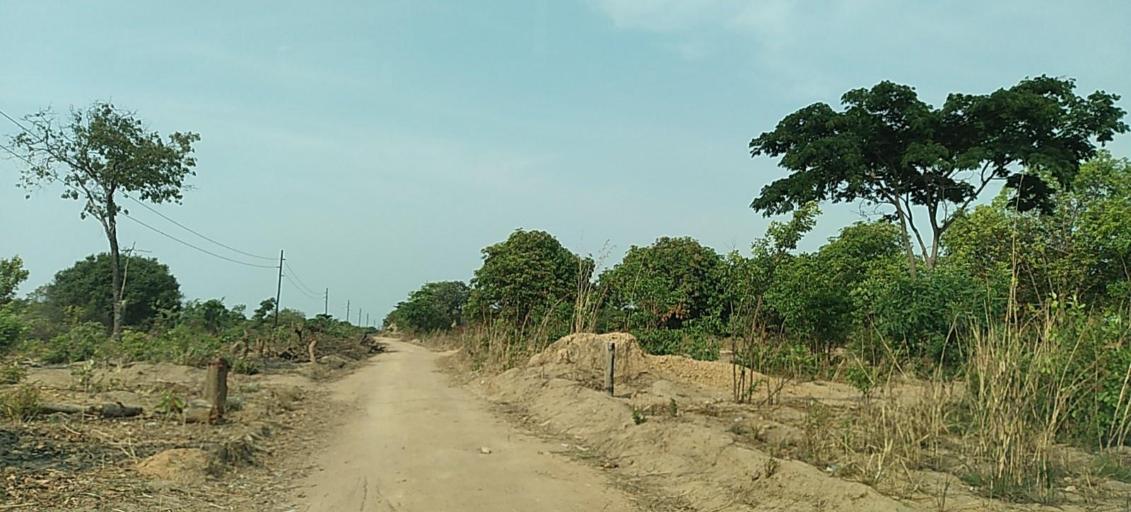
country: ZM
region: Copperbelt
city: Ndola
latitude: -13.2196
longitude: 28.6800
